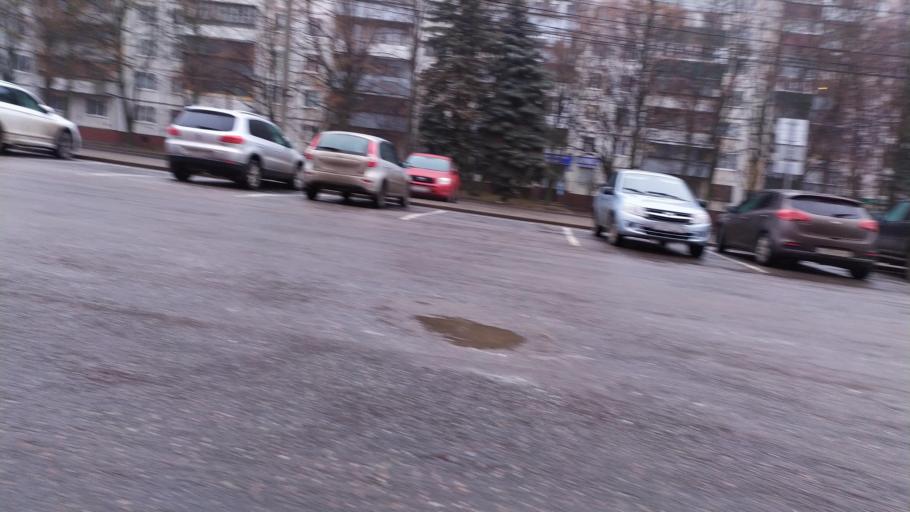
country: RU
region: Kursk
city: Kursk
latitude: 51.7420
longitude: 36.1353
